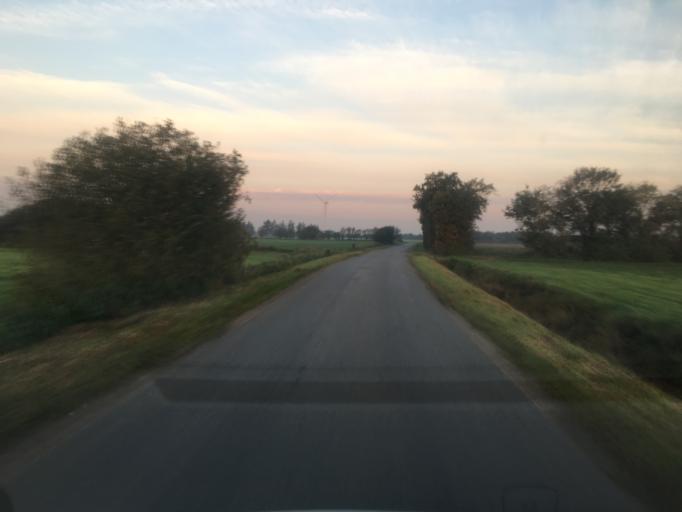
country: DK
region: South Denmark
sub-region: Tonder Kommune
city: Logumkloster
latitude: 54.9854
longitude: 9.0569
